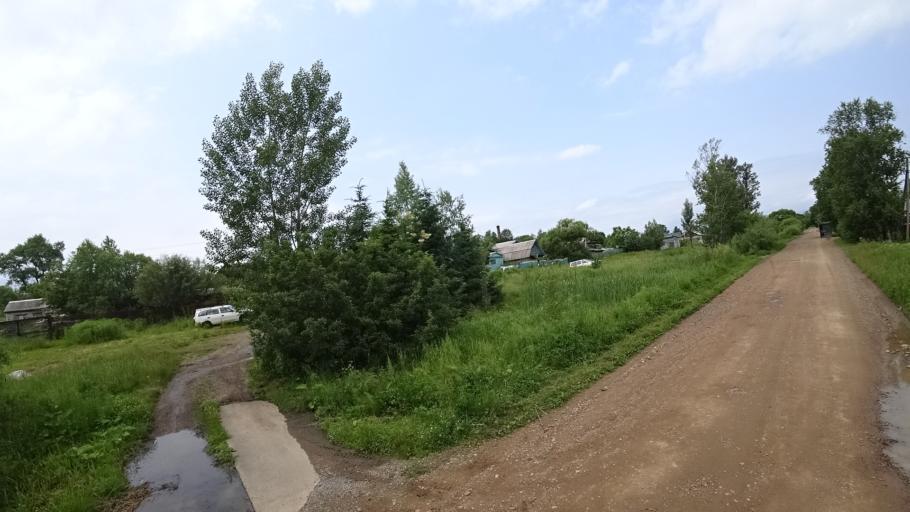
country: RU
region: Primorskiy
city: Novosysoyevka
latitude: 44.2277
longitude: 133.3673
